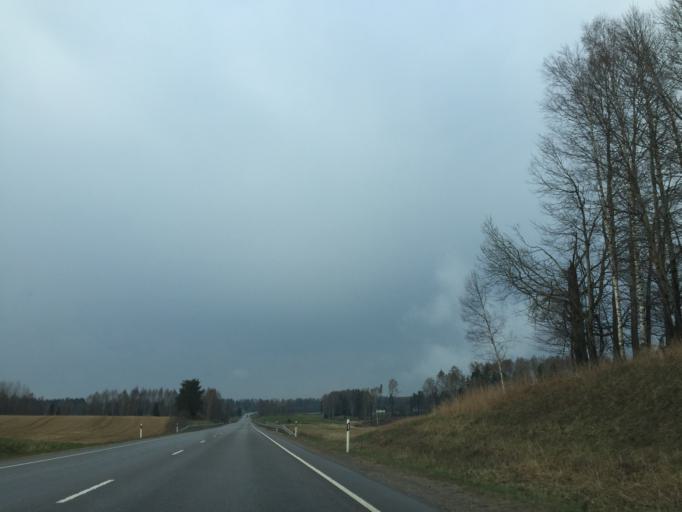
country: EE
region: Tartu
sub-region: UElenurme vald
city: Ulenurme
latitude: 58.1626
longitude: 26.6926
